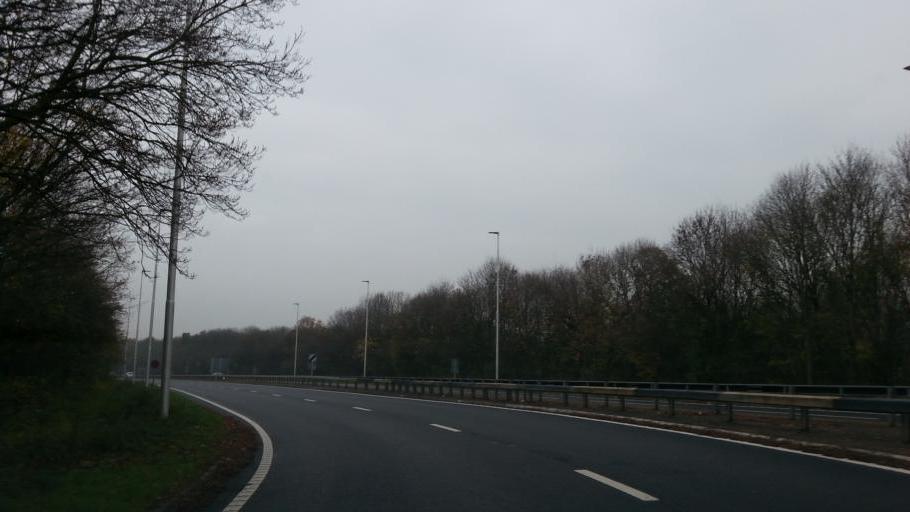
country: GB
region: England
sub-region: Cambridgeshire
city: Yaxley
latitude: 52.5376
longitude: -0.3032
